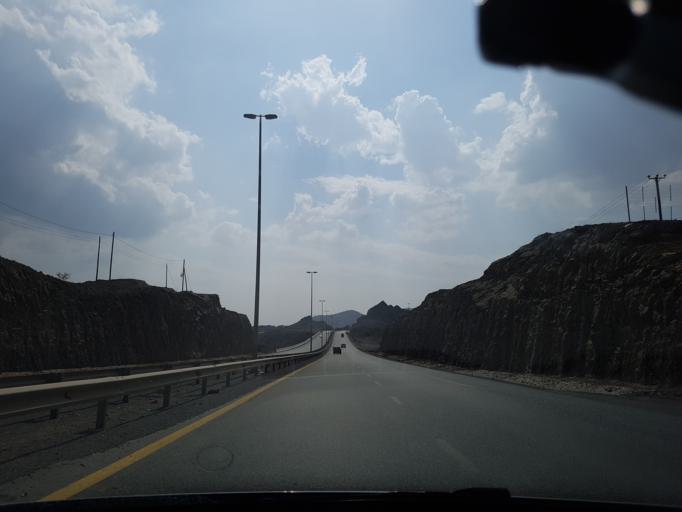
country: AE
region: Al Fujayrah
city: Dibba Al-Fujairah
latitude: 25.5292
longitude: 56.1180
